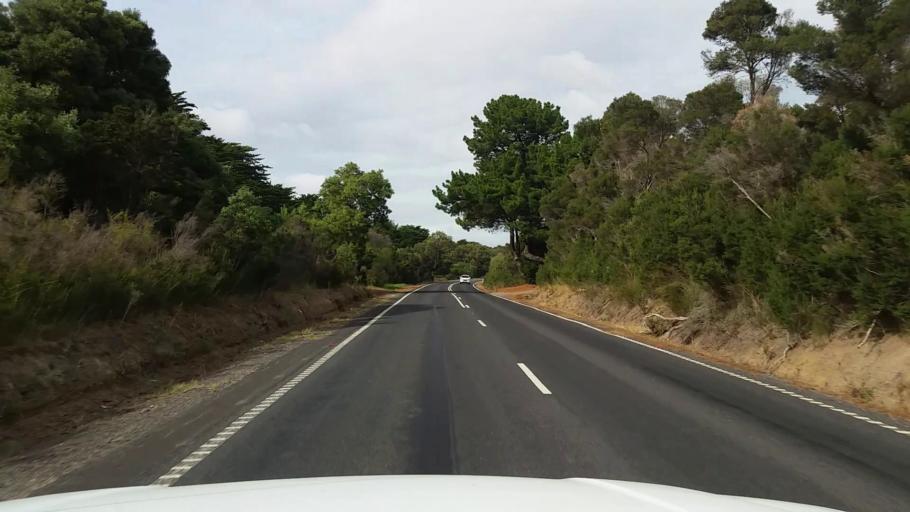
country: AU
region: Victoria
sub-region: Mornington Peninsula
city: Merricks
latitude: -38.3156
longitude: 145.0878
